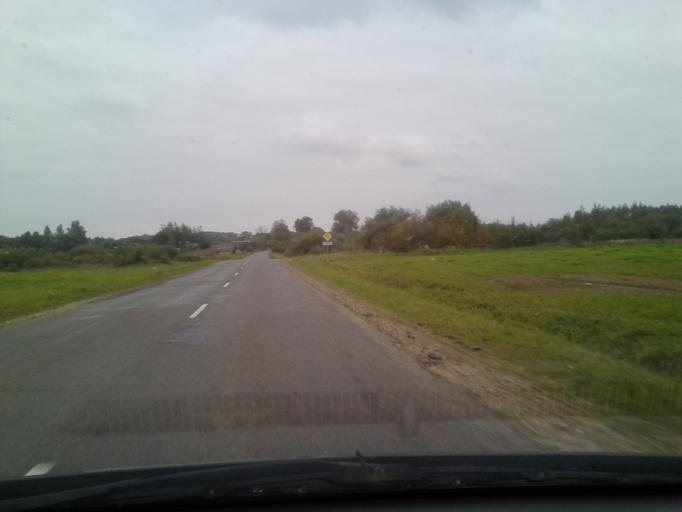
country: BY
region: Vitebsk
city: Pastavy
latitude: 55.1207
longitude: 26.9264
